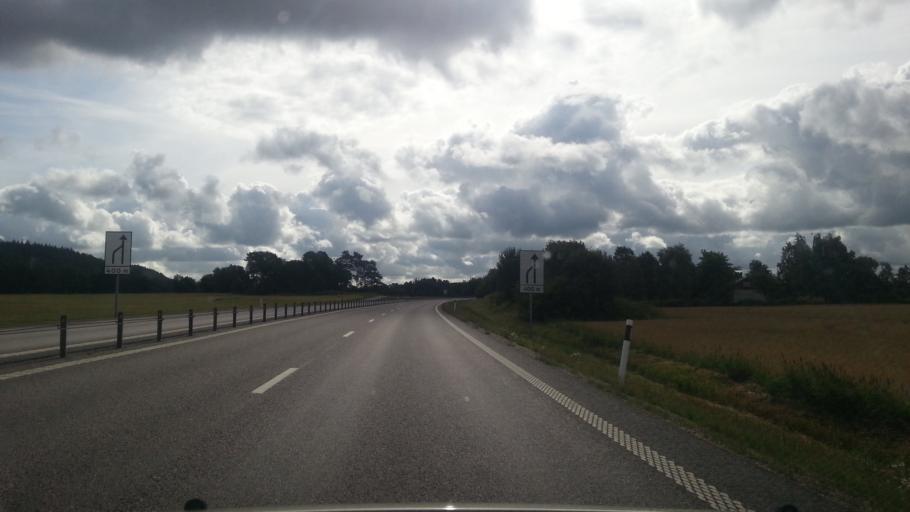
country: SE
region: Vaestra Goetaland
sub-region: Vanersborgs Kommun
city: Vargon
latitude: 58.2874
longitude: 12.4170
